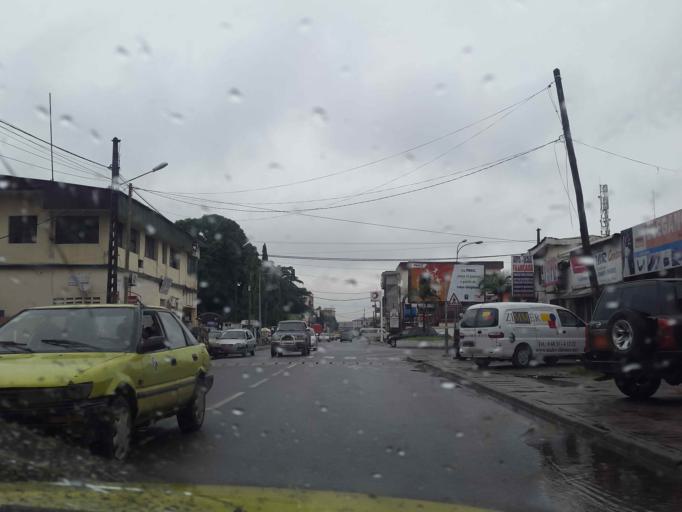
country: CM
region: Littoral
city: Douala
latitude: 4.0361
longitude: 9.6941
